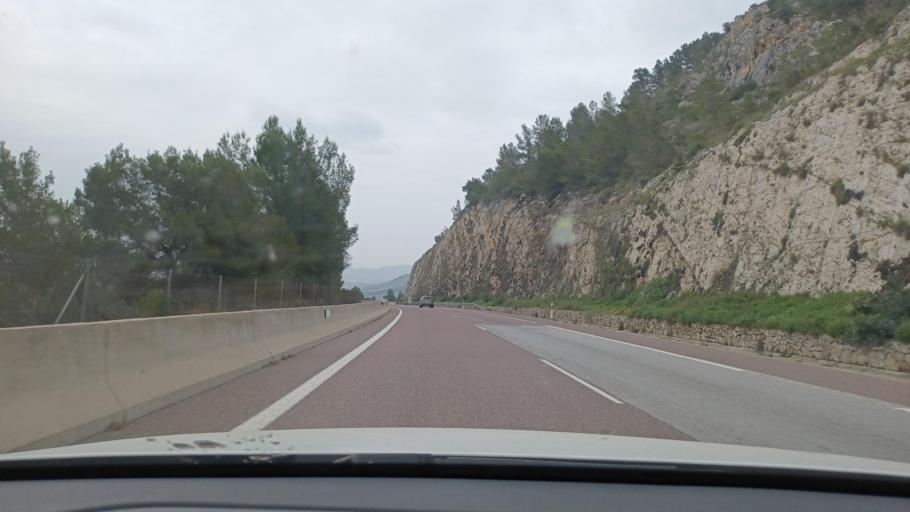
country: ES
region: Valencia
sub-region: Provincia de Valencia
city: L'Olleria
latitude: 38.9295
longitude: -0.5740
